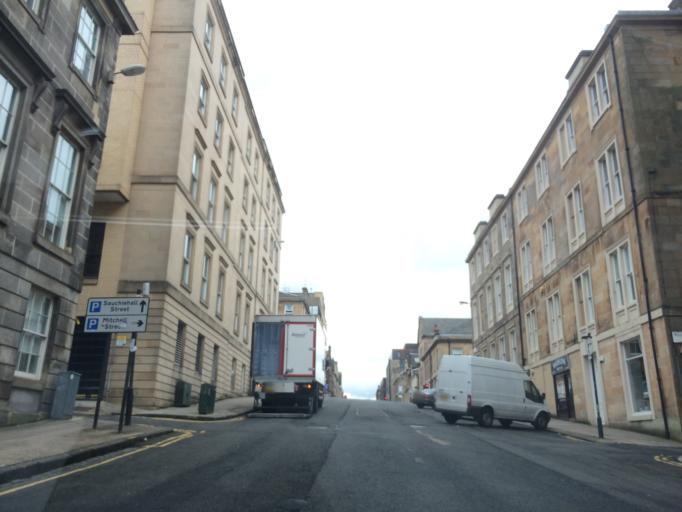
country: GB
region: Scotland
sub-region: Glasgow City
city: Glasgow
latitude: 55.8623
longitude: -4.2613
